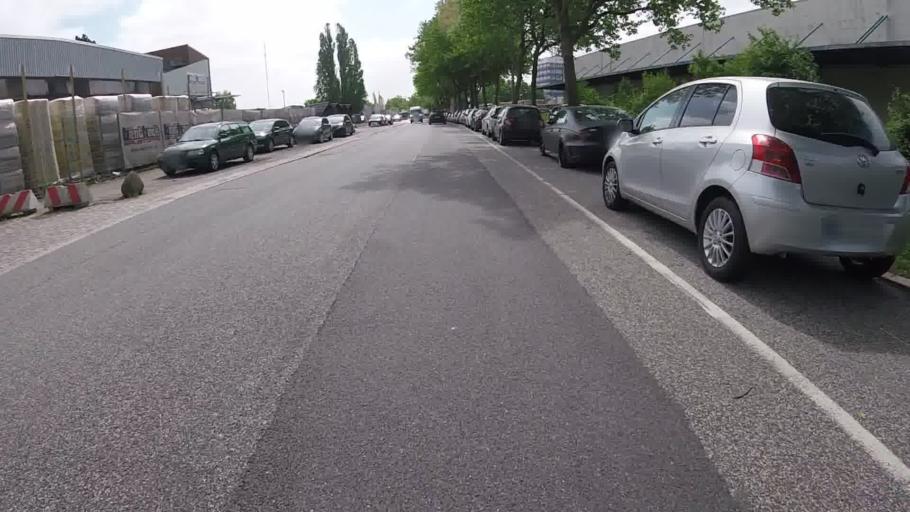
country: DE
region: Hamburg
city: Rothenburgsort
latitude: 53.5261
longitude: 10.0804
